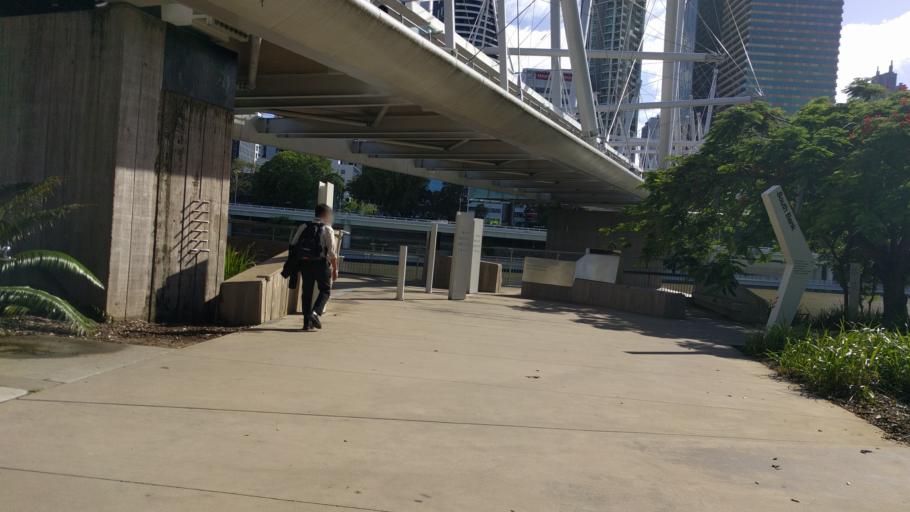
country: AU
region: Queensland
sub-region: Brisbane
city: Spring Hill
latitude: -27.4698
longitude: 153.0170
